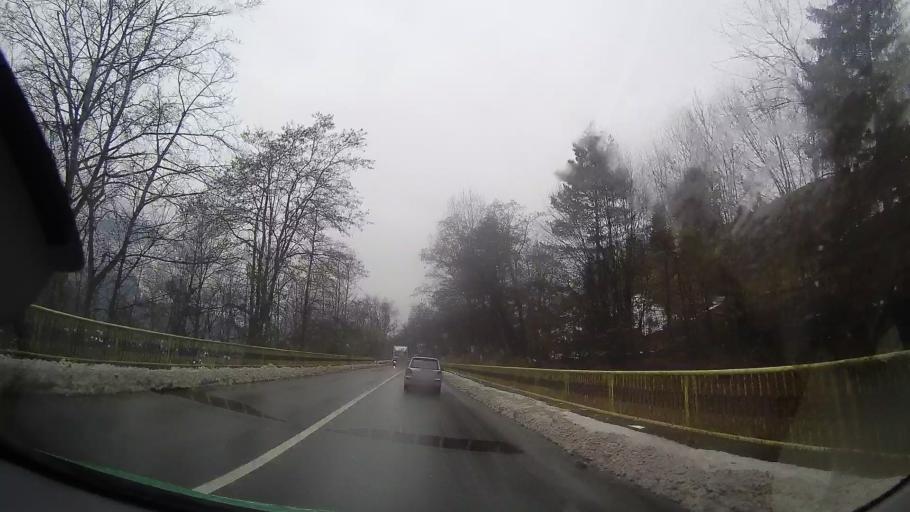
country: RO
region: Neamt
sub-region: Comuna Bicaz
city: Dodeni
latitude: 46.9021
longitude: 26.1162
